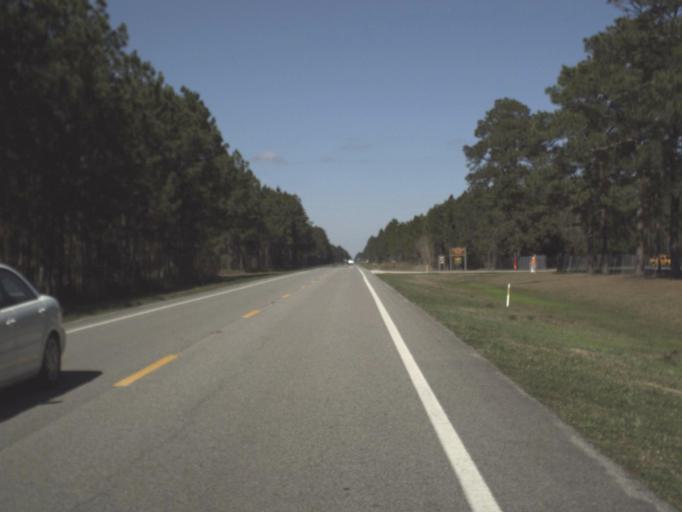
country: US
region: Florida
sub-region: Gulf County
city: Port Saint Joe
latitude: 29.9014
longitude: -85.2103
